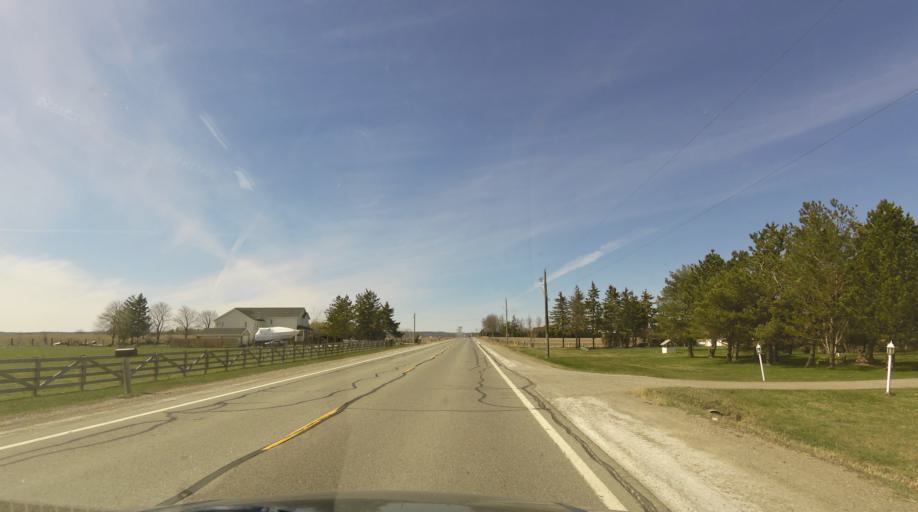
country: CA
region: Ontario
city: Brampton
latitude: 43.7098
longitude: -79.8877
